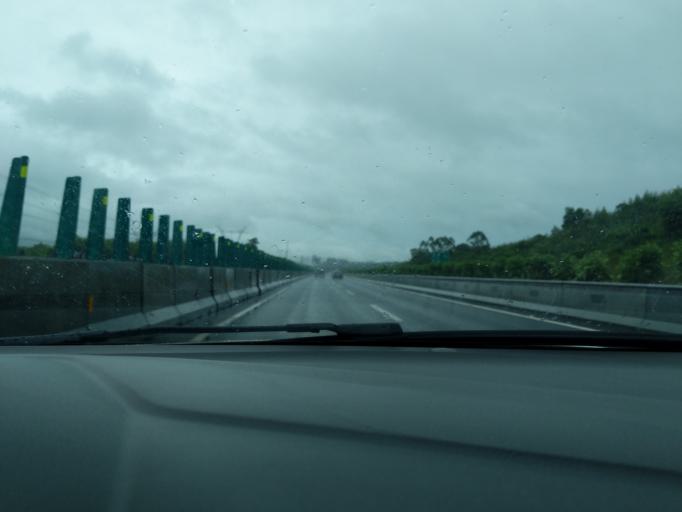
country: CN
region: Guangdong
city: Pingshi
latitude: 22.2597
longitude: 112.3140
